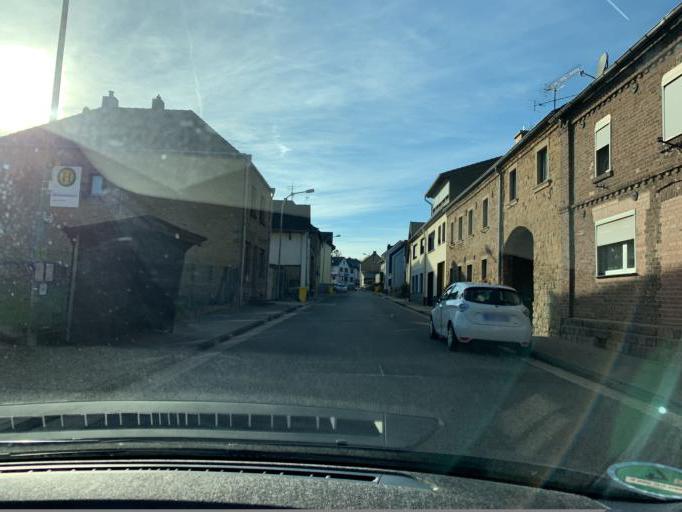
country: DE
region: North Rhine-Westphalia
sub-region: Regierungsbezirk Koln
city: Nideggen
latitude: 50.6809
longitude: 6.5215
